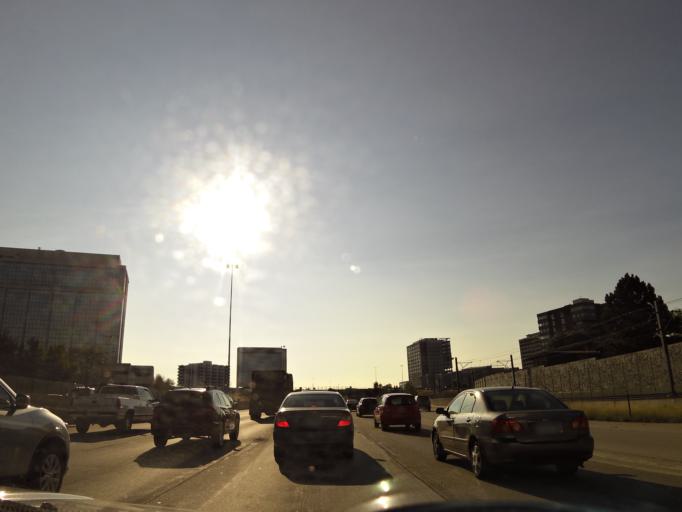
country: US
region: Colorado
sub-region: Arapahoe County
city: Glendale
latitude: 39.6839
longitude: -104.9445
